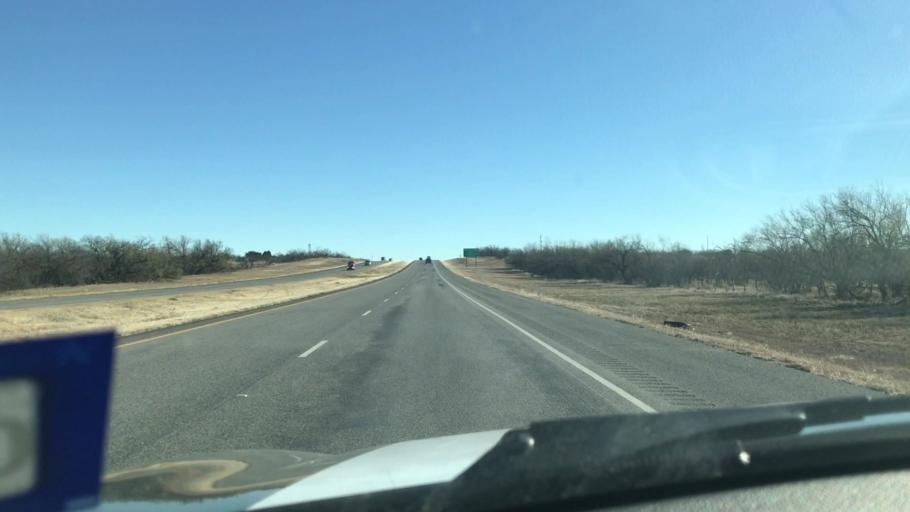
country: US
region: Texas
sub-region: Scurry County
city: Snyder
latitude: 32.7618
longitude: -100.9326
